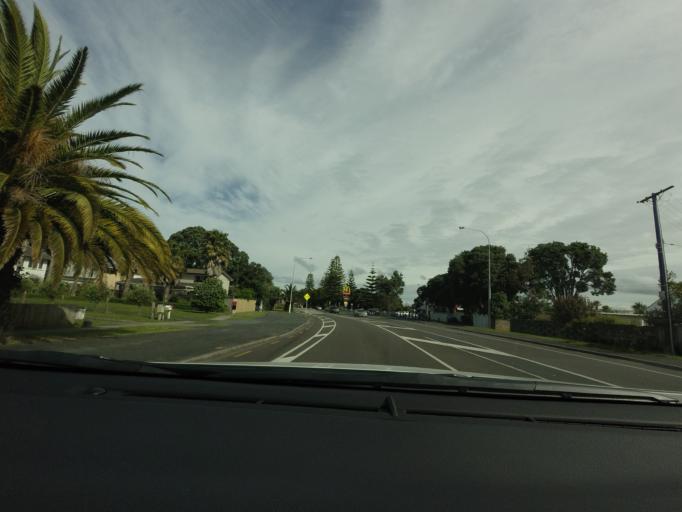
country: NZ
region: Auckland
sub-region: Auckland
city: Rothesay Bay
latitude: -36.5841
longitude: 174.6944
